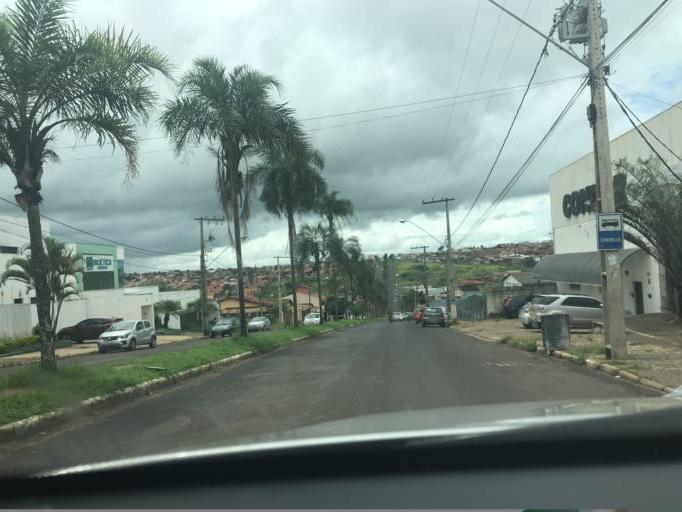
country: BR
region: Minas Gerais
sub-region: Araxa
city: Araxa
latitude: -19.5798
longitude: -46.9344
